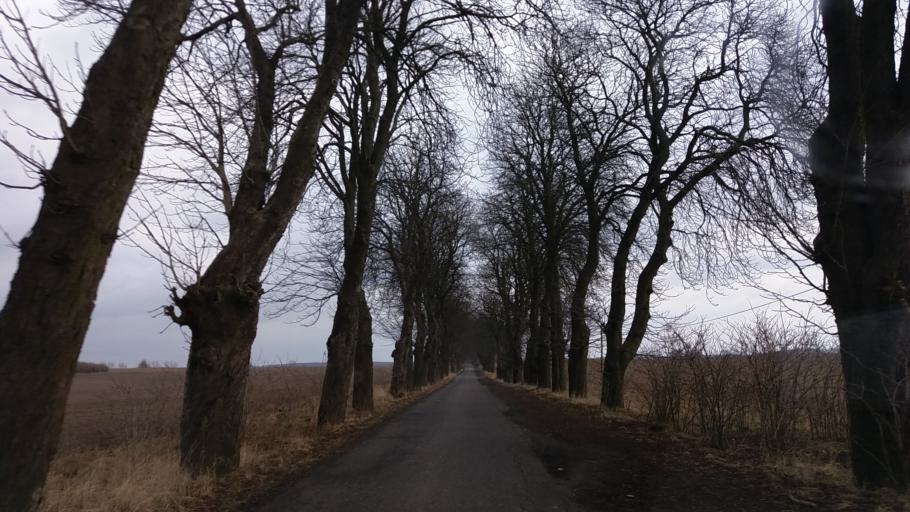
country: PL
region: West Pomeranian Voivodeship
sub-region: Powiat choszczenski
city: Recz
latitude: 53.2551
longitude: 15.5962
